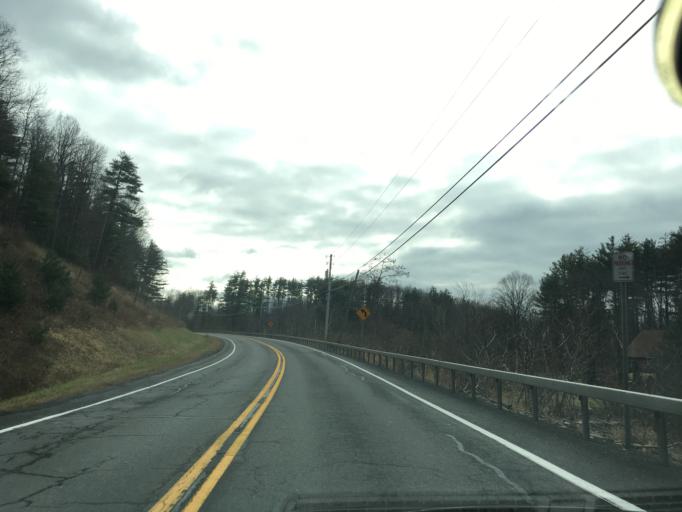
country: US
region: New York
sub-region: Rensselaer County
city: Averill Park
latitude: 42.6067
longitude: -73.5215
